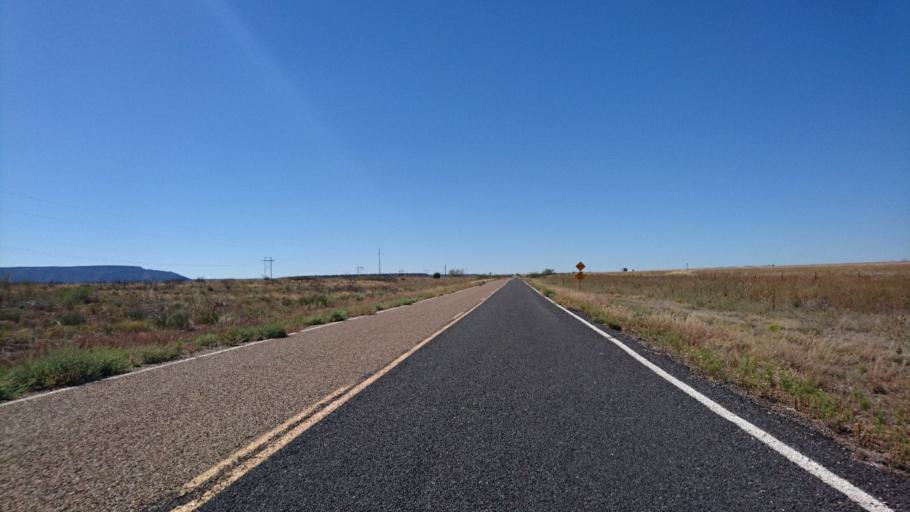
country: US
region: New Mexico
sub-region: Quay County
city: Tucumcari
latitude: 35.0866
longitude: -104.0963
